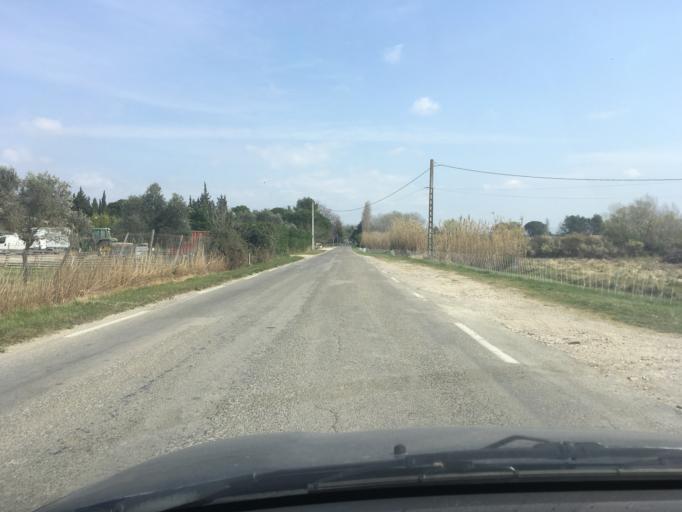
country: FR
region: Provence-Alpes-Cote d'Azur
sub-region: Departement du Vaucluse
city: Aubignan
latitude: 44.1004
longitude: 5.0046
